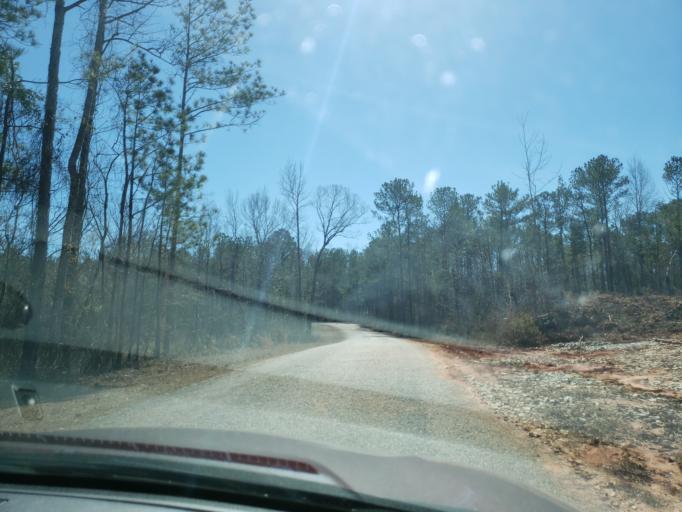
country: US
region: Alabama
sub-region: Elmore County
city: Tallassee
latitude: 32.6639
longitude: -85.8699
